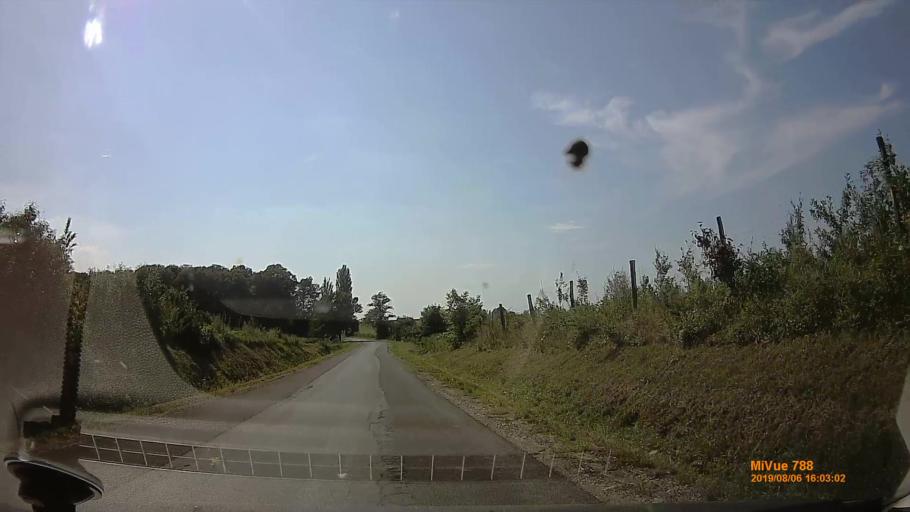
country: HU
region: Zala
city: Murakeresztur
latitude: 46.3049
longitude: 16.9707
